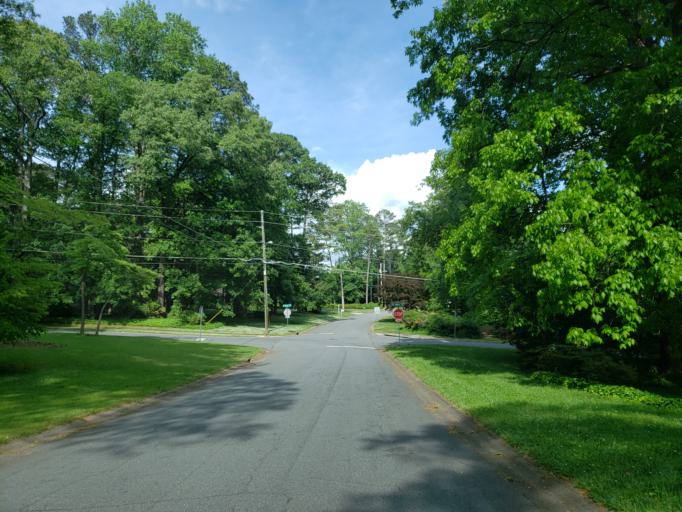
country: US
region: Georgia
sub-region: Cobb County
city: Marietta
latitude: 33.9622
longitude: -84.5635
